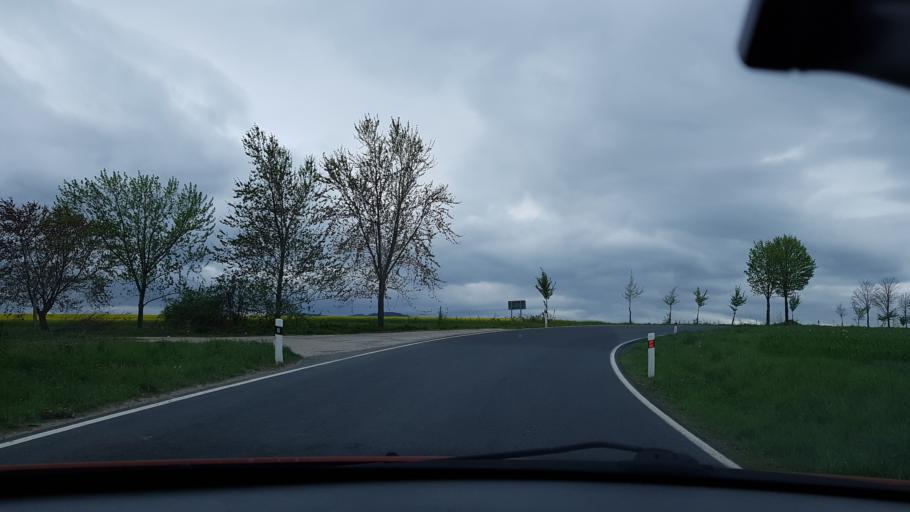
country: CZ
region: Olomoucky
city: Mikulovice
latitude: 50.3077
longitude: 17.3133
